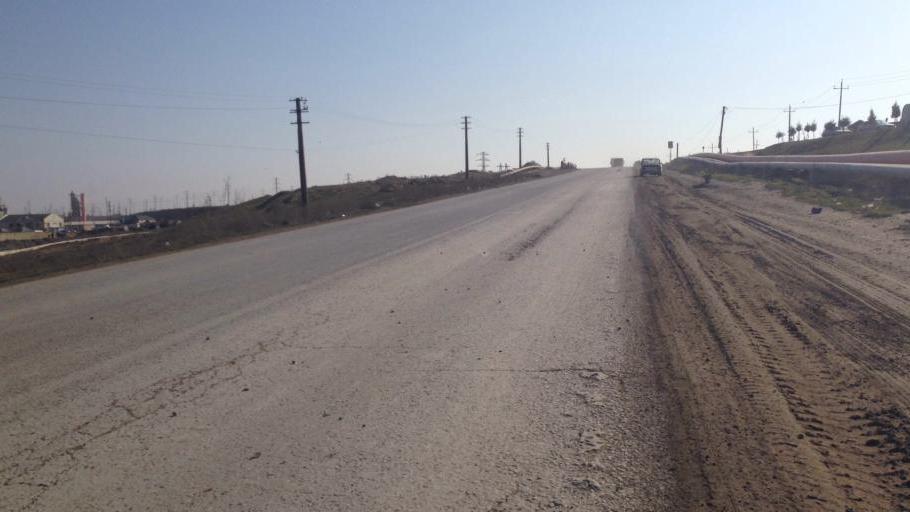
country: AZ
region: Baki
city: Balakhani
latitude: 40.4645
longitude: 49.8881
